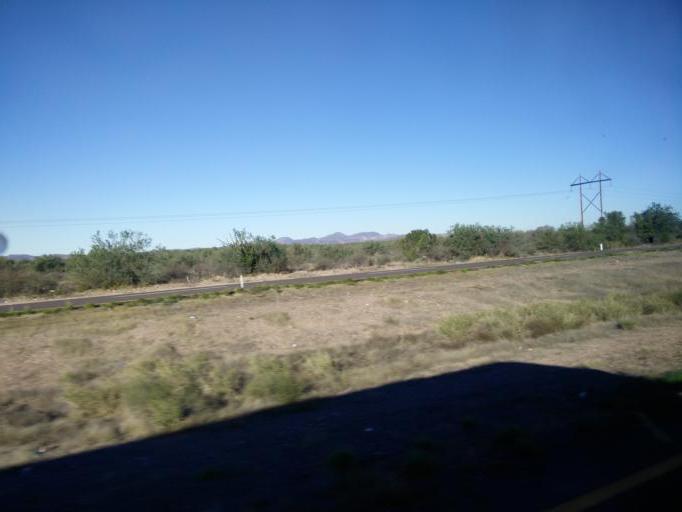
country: MX
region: Sonora
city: Heroica Guaymas
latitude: 28.1429
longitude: -110.9744
